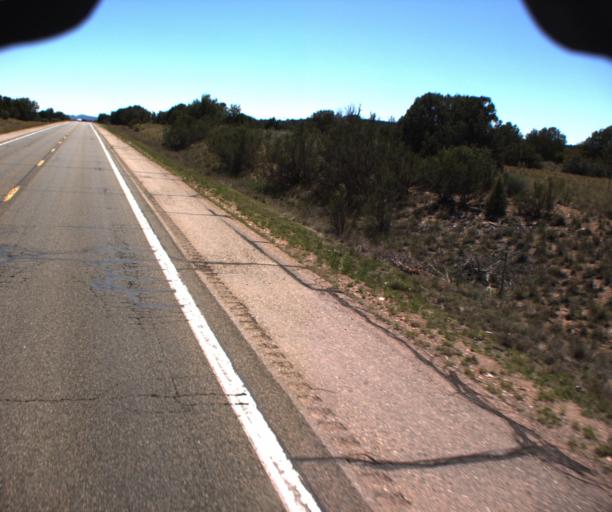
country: US
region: Arizona
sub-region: Yavapai County
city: Paulden
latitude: 34.9519
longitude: -112.4212
